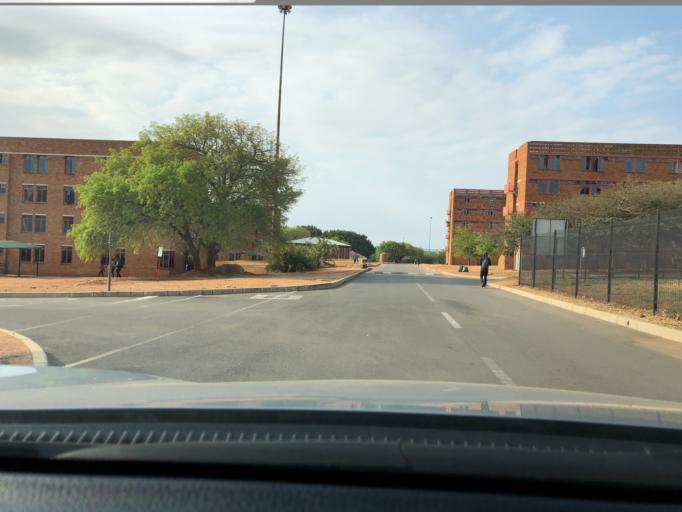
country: ZA
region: Limpopo
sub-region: Capricorn District Municipality
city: Mankoeng
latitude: -23.8919
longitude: 29.7355
